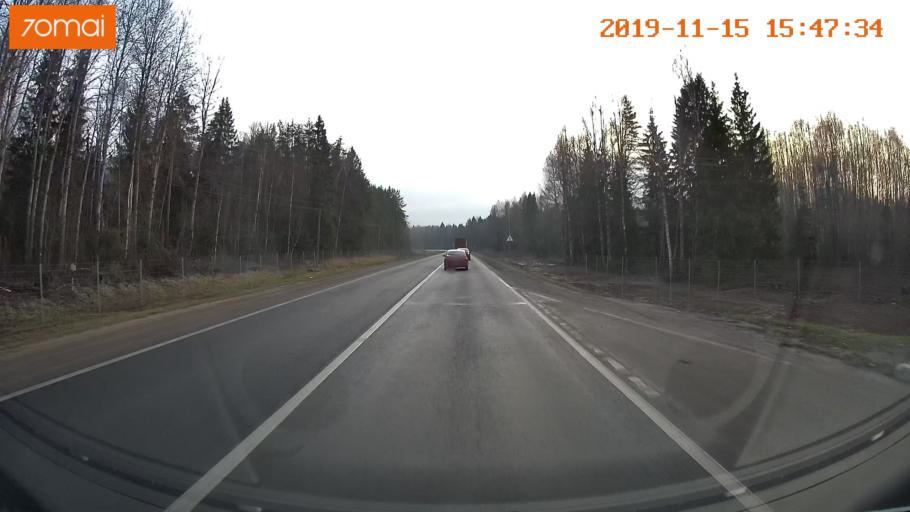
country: RU
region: Jaroslavl
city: Danilov
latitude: 57.9368
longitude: 40.0087
